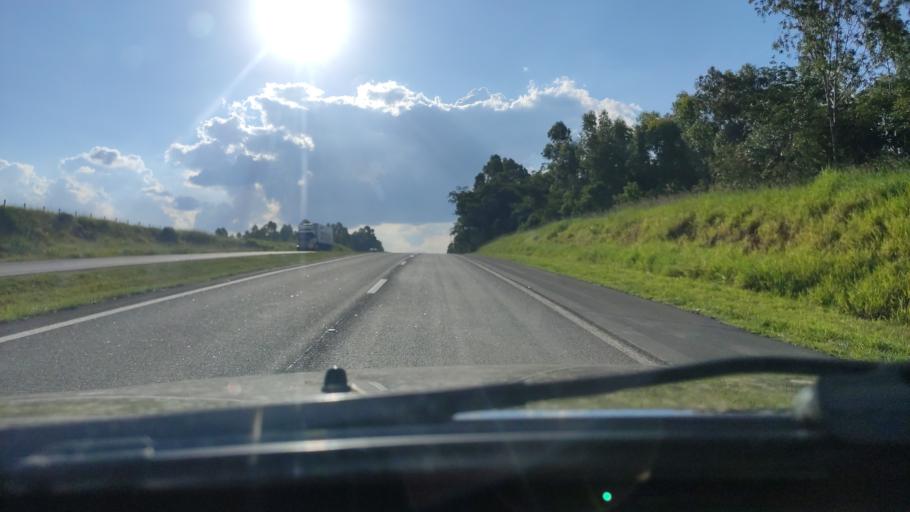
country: BR
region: Sao Paulo
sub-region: Itapira
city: Itapira
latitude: -22.4517
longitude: -46.8750
